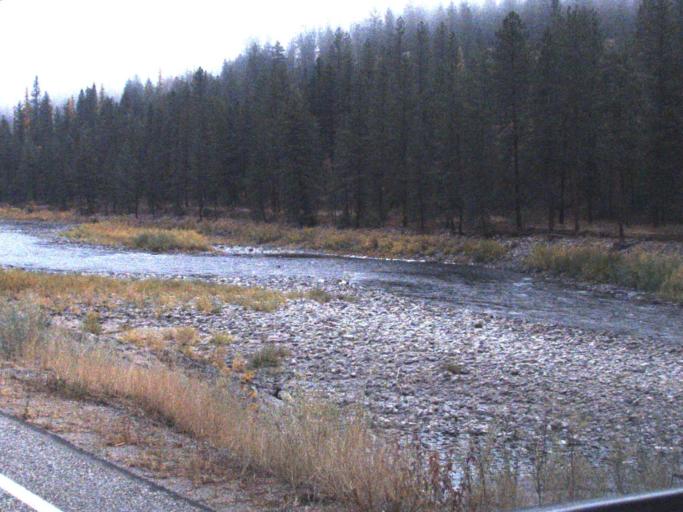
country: US
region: Washington
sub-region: Stevens County
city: Kettle Falls
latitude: 48.8243
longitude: -118.1710
